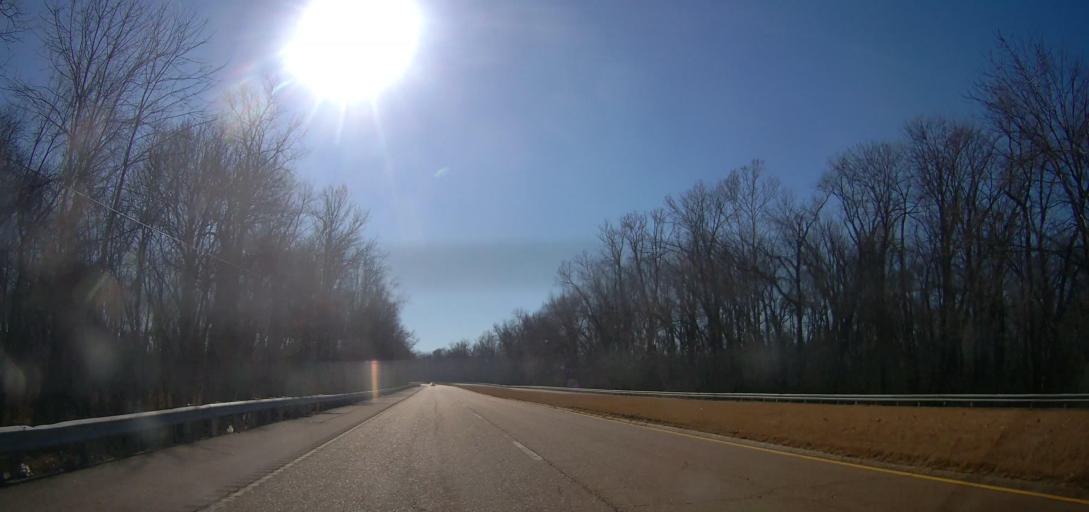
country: US
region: Tennessee
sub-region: Shelby County
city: Millington
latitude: 35.2815
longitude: -89.8853
